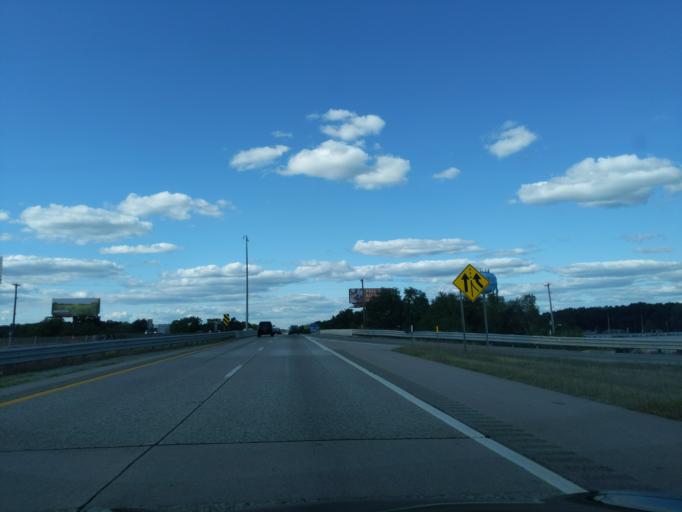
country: US
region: Michigan
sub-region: Muskegon County
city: Muskegon Heights
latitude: 43.2187
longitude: -86.2049
